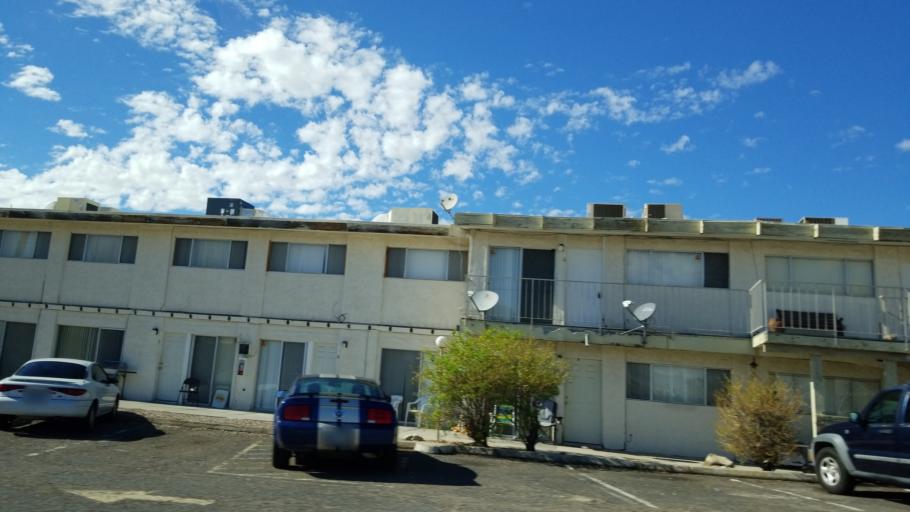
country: US
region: Arizona
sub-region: Mohave County
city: Lake Havasu City
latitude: 34.4794
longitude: -114.3178
